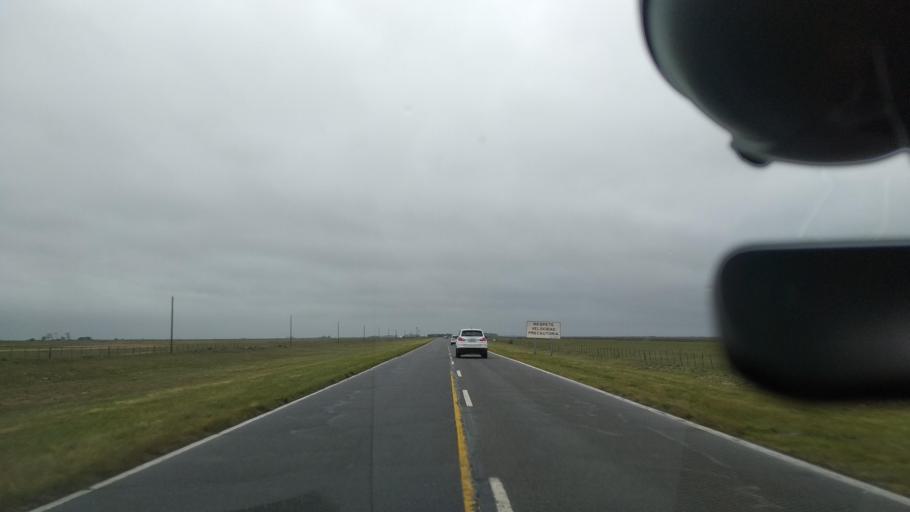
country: AR
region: Buenos Aires
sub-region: Partido de Dolores
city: Dolores
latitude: -36.0945
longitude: -57.4349
